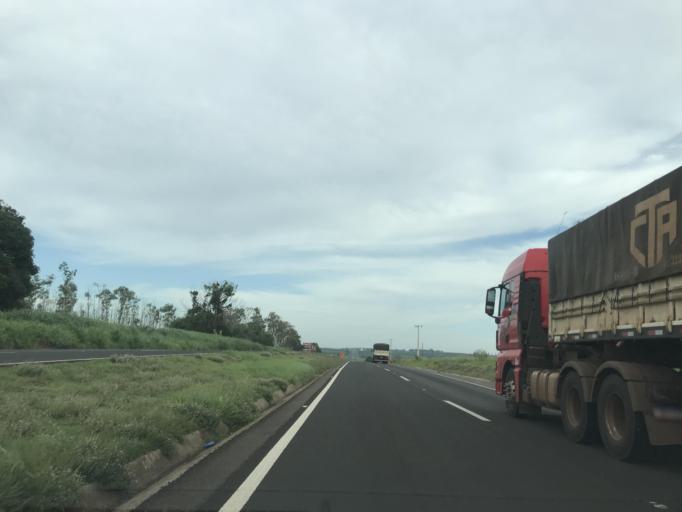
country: BR
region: Parana
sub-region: Alto Parana
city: Alto Parana
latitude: -23.1184
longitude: -52.3195
